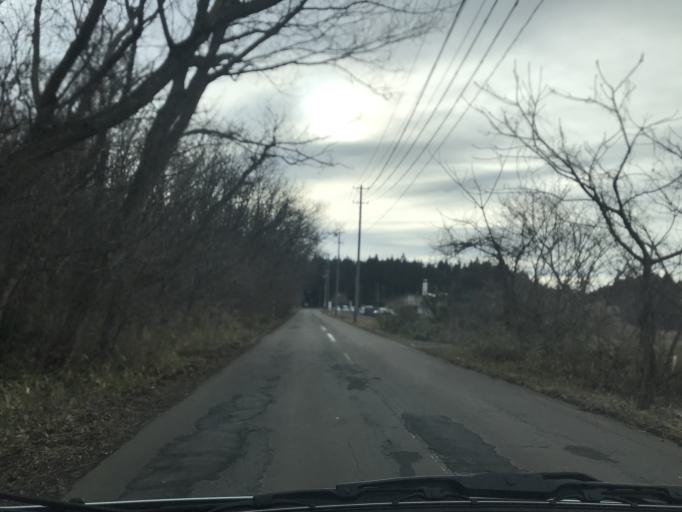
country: JP
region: Iwate
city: Kitakami
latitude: 39.2418
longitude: 141.0732
